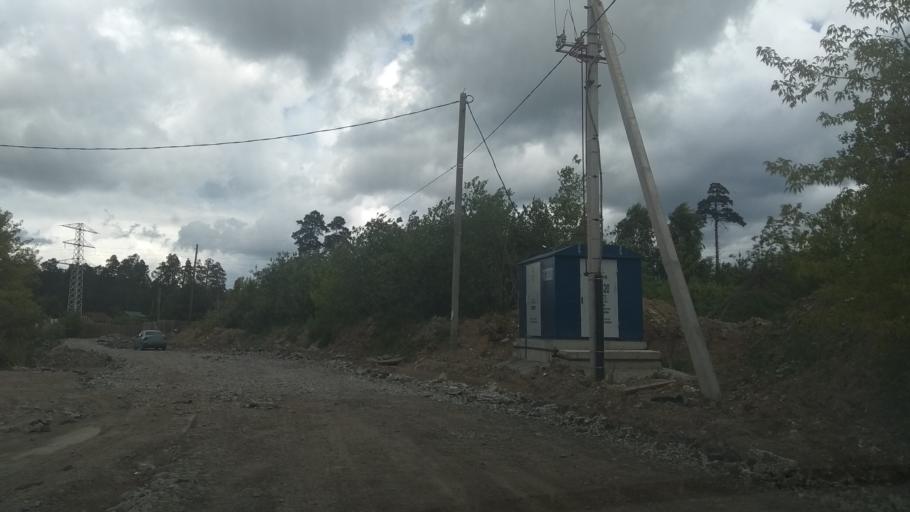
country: RU
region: Sverdlovsk
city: Verkhnyaya Pyshma
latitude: 56.9197
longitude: 60.5718
